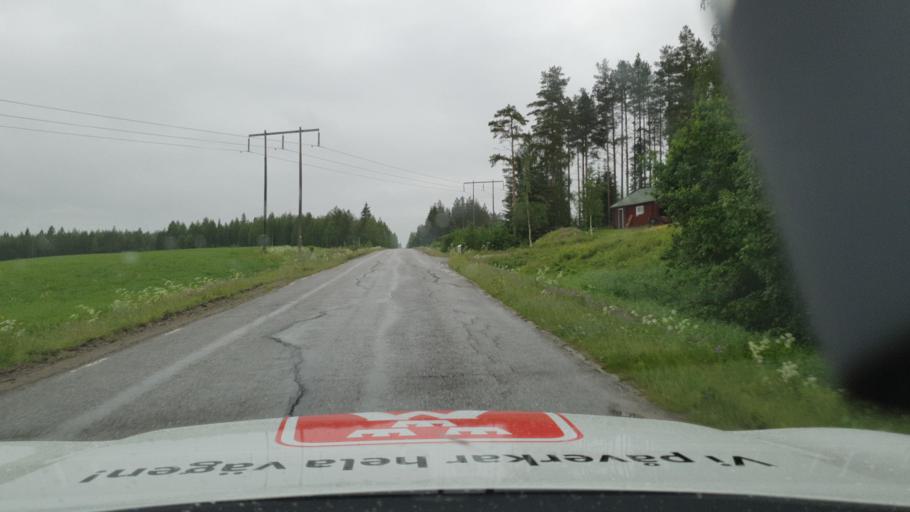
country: SE
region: Vaesterbotten
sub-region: Nordmalings Kommun
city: Nordmaling
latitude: 63.8130
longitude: 19.4989
